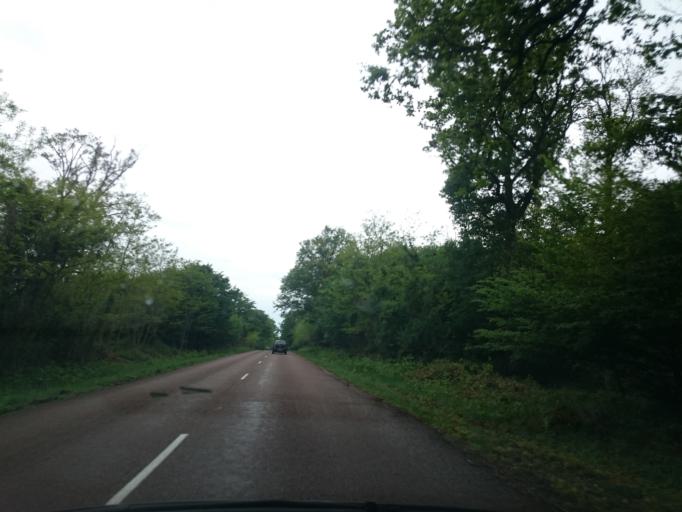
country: FR
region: Centre
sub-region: Departement du Loir-et-Cher
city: Saint-Dye-sur-Loire
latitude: 47.6280
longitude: 1.5128
